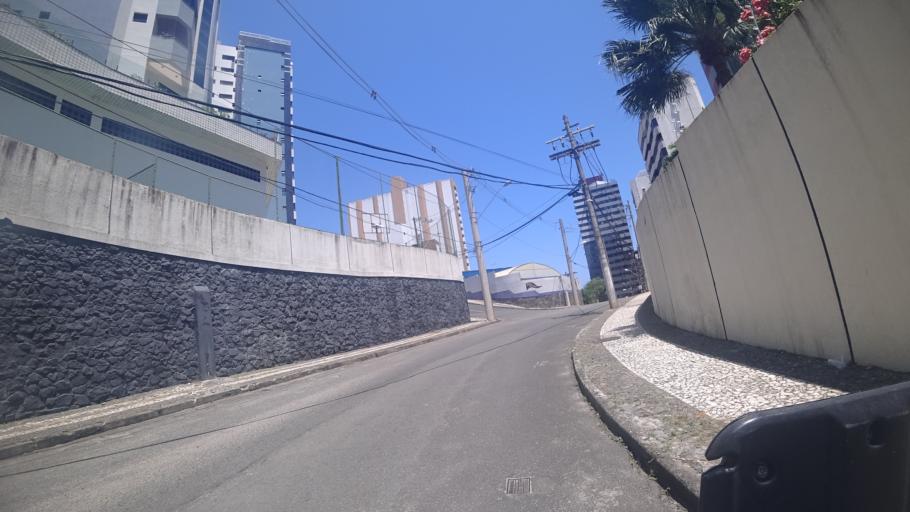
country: BR
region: Bahia
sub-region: Salvador
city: Salvador
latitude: -12.9869
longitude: -38.4626
